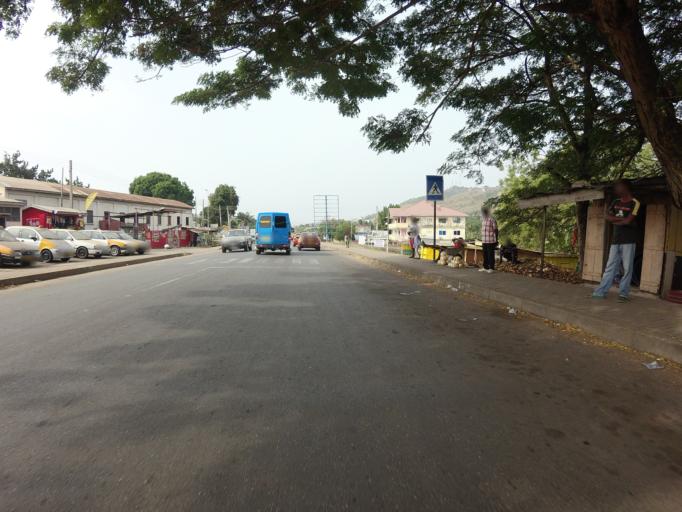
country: GH
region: Volta
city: Ho
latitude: 6.6113
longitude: 0.4606
